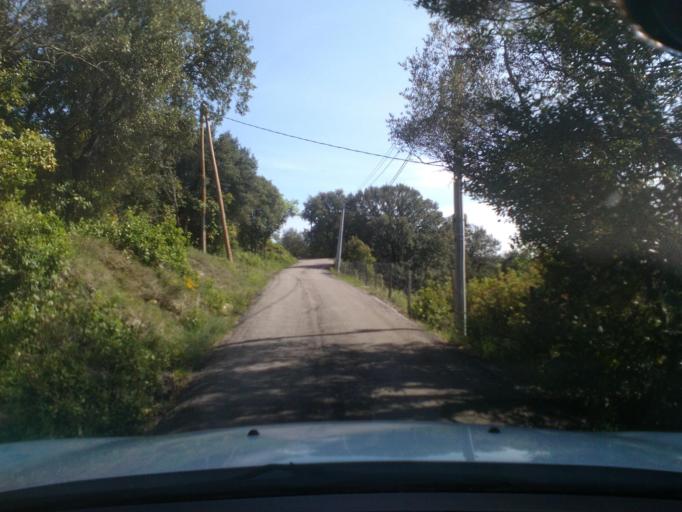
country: FR
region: Languedoc-Roussillon
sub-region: Departement du Gard
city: Saint-Hippolyte-du-Fort
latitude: 43.9975
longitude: 3.8802
